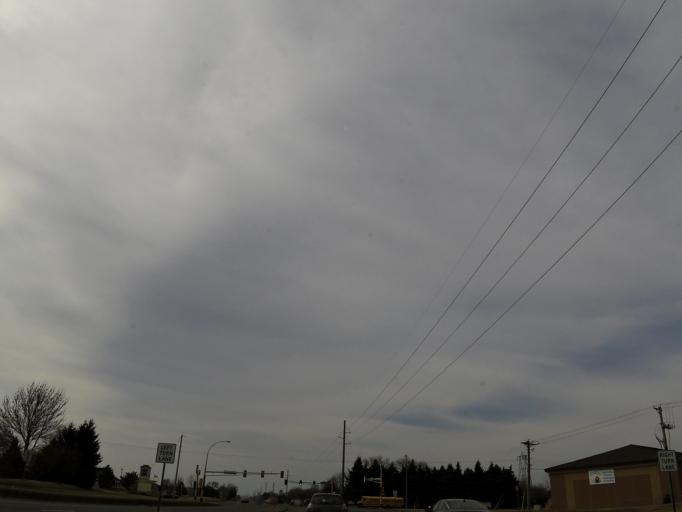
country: US
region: Minnesota
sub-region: Dakota County
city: Rosemount
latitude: 44.7318
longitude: -93.1545
